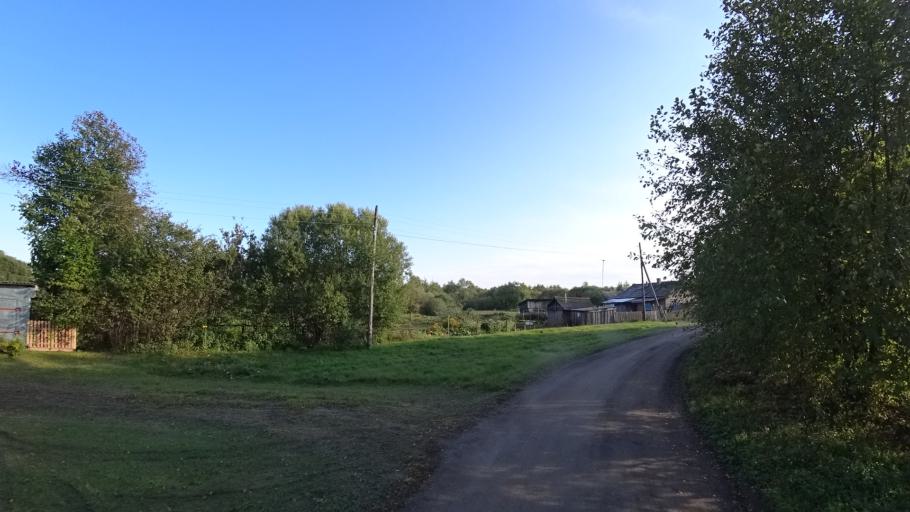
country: RU
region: Amur
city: Arkhara
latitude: 49.3615
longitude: 130.1291
